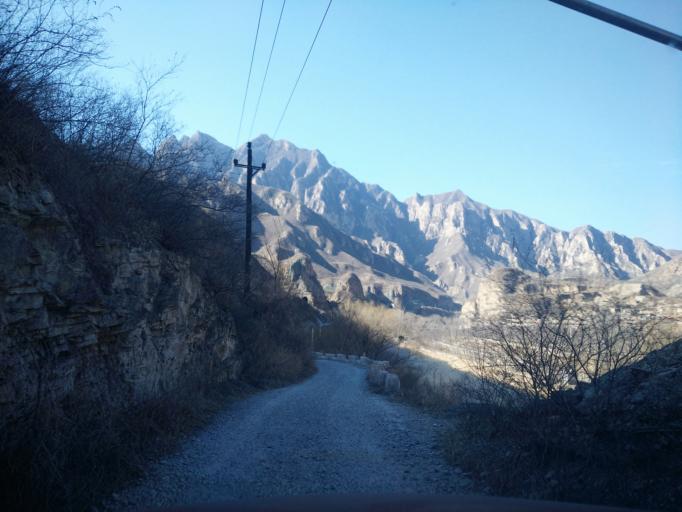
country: CN
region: Beijing
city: Yanjiatai
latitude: 40.1676
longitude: 115.6597
